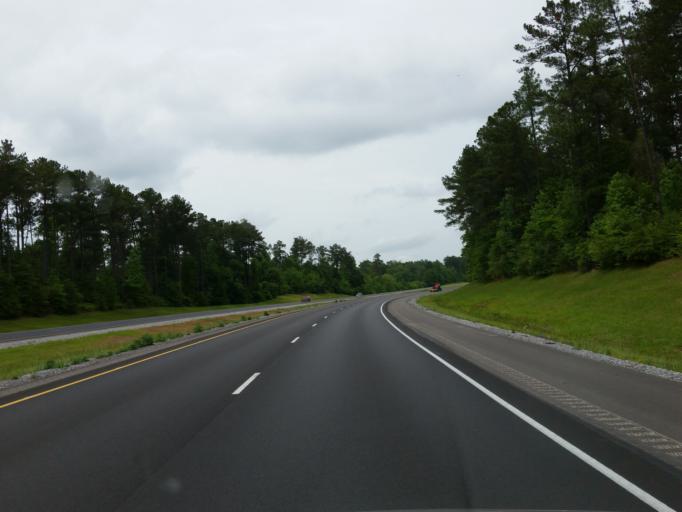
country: US
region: Mississippi
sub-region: Jones County
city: Sharon
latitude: 31.8728
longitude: -89.0453
